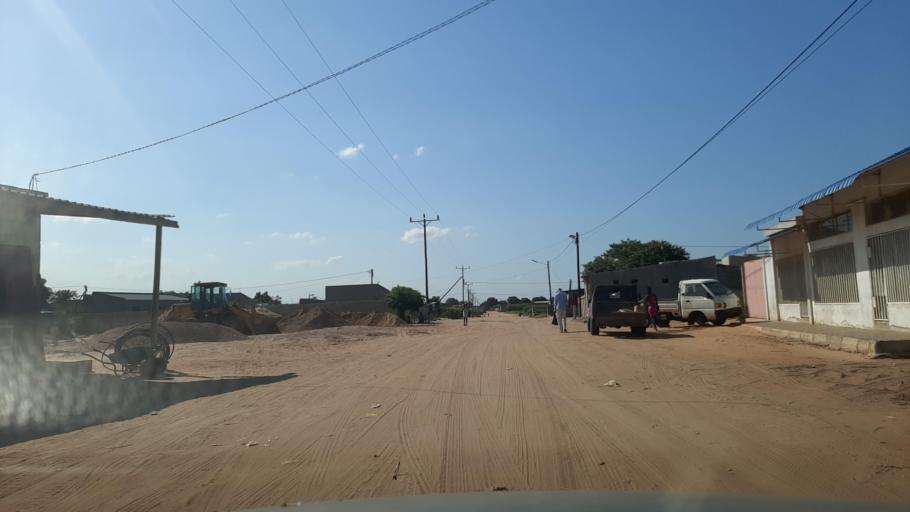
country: MZ
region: Maputo
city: Matola
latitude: -25.7982
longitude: 32.4905
